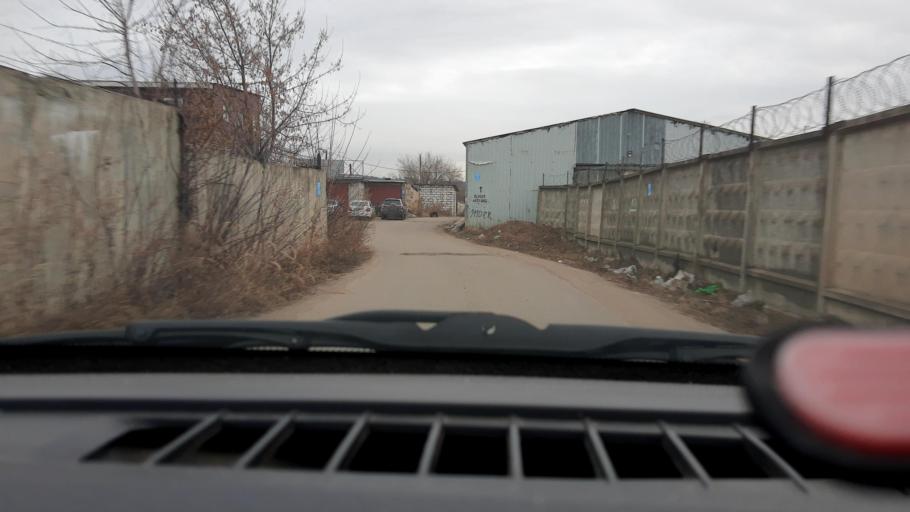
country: RU
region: Nizjnij Novgorod
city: Nizhniy Novgorod
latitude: 56.2645
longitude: 43.9429
